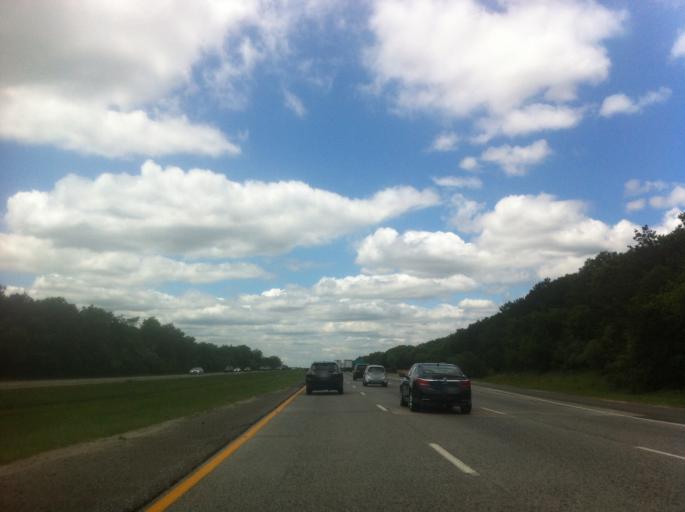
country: US
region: New York
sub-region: Suffolk County
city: Gordon Heights
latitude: 40.8256
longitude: -72.9574
